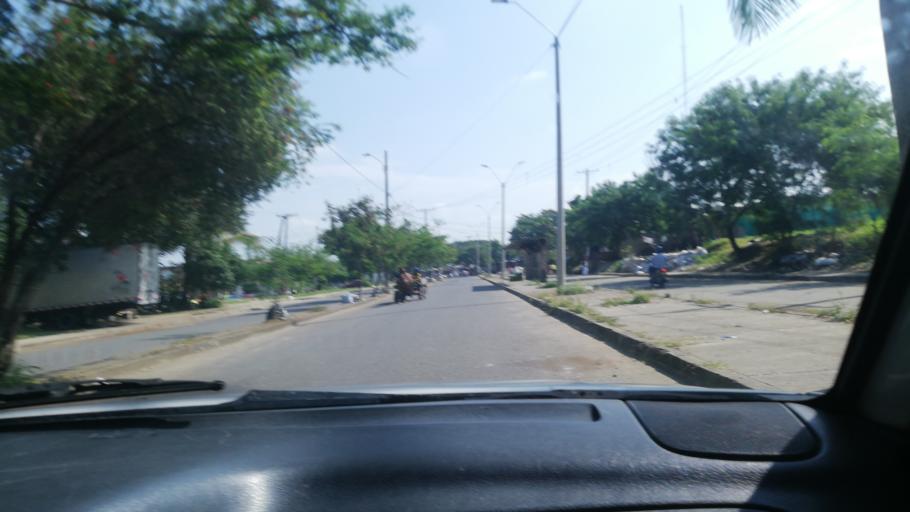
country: CO
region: Valle del Cauca
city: Cali
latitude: 3.4132
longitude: -76.4852
